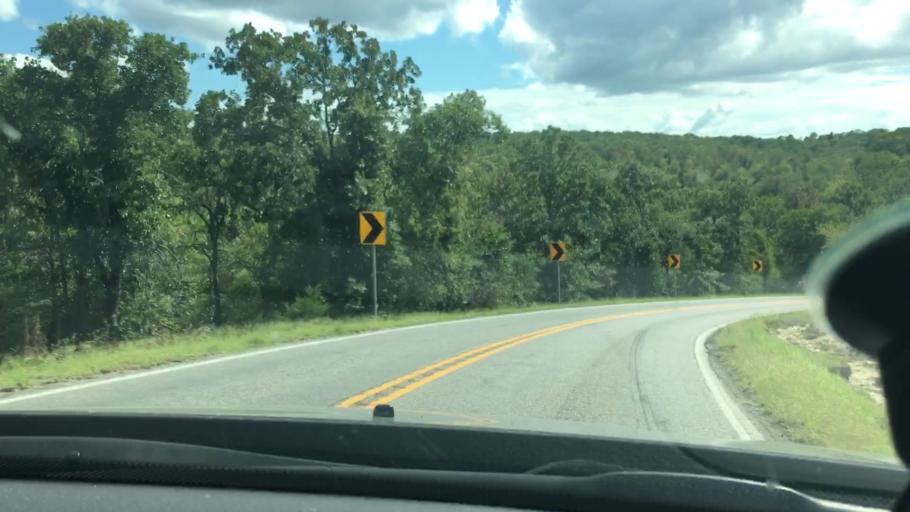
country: US
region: Oklahoma
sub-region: Sequoyah County
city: Vian
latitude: 35.6181
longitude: -94.9620
